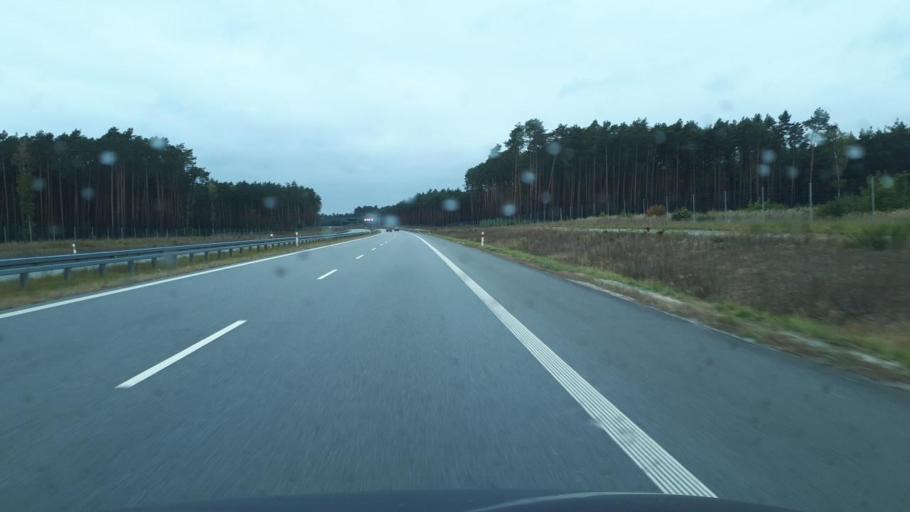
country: PL
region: Greater Poland Voivodeship
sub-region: Powiat kepinski
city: Kepno
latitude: 51.3266
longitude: 17.9890
